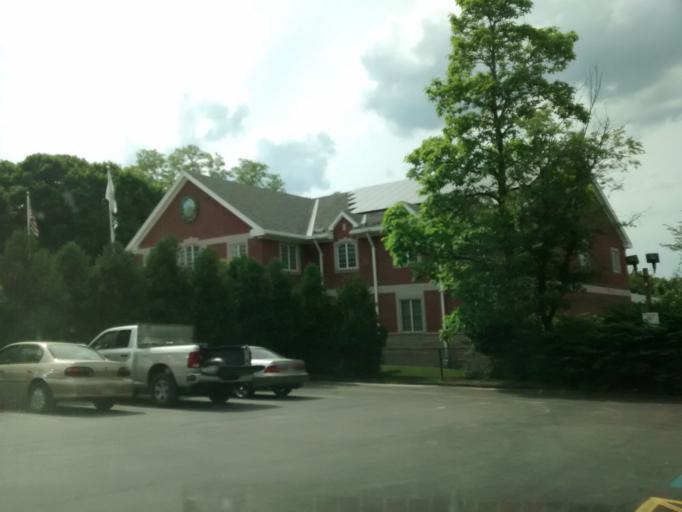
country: US
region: Massachusetts
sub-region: Middlesex County
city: Hopkinton
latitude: 42.2286
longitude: -71.5231
